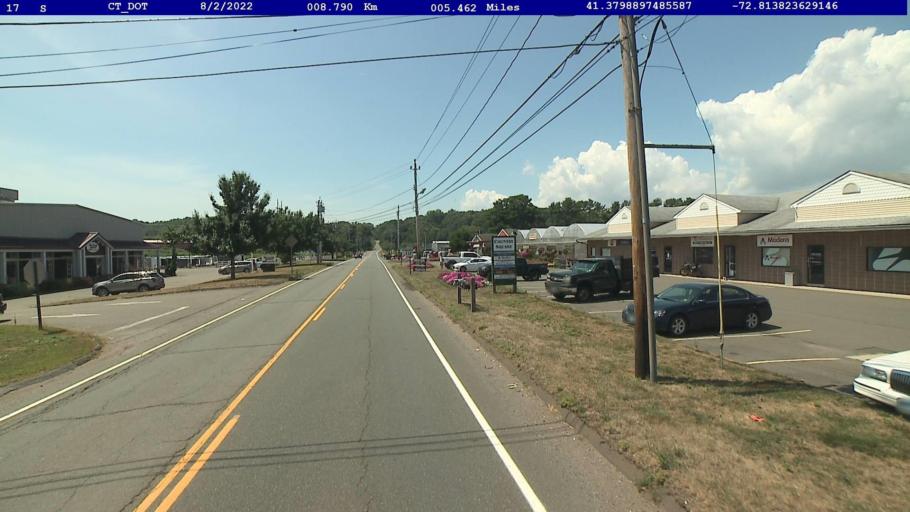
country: US
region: Connecticut
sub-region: New Haven County
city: North Haven
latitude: 41.3792
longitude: -72.8138
